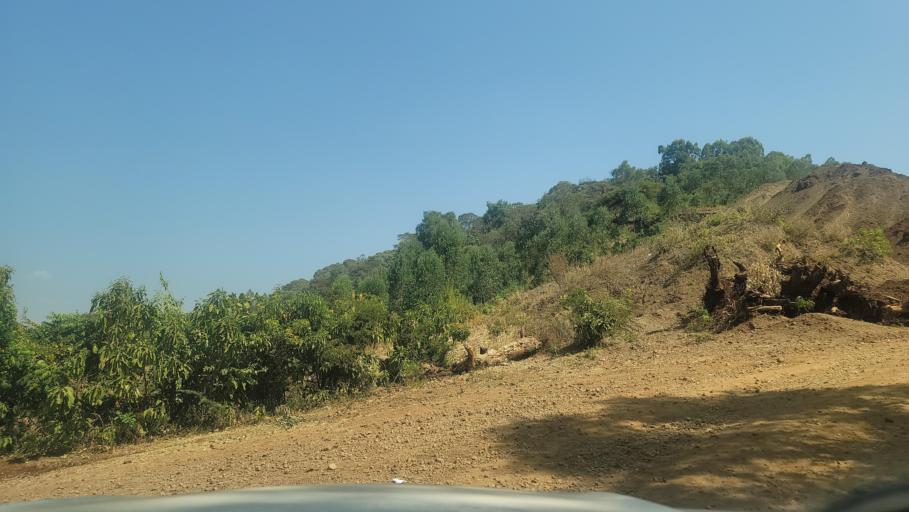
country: ET
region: Oromiya
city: Agaro
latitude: 7.8507
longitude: 36.5391
